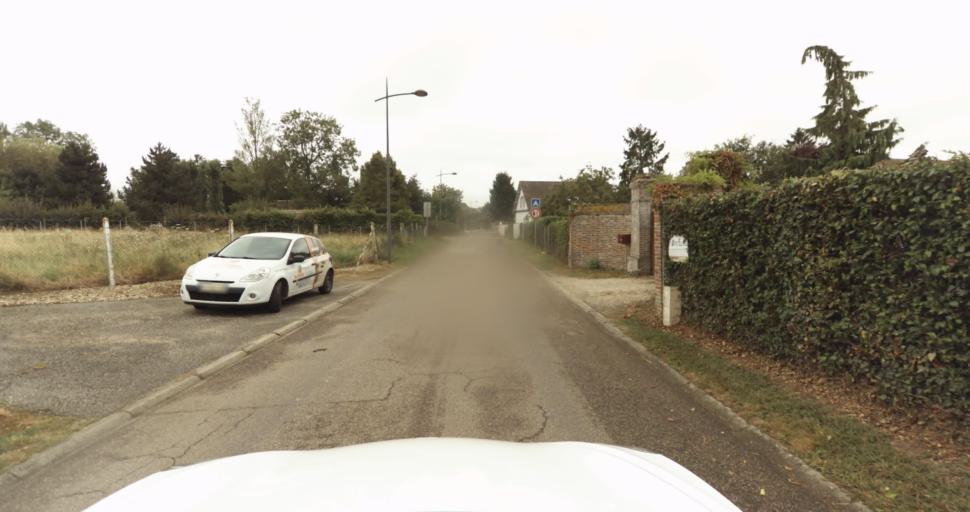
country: FR
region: Haute-Normandie
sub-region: Departement de l'Eure
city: Aviron
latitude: 49.0681
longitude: 1.0711
